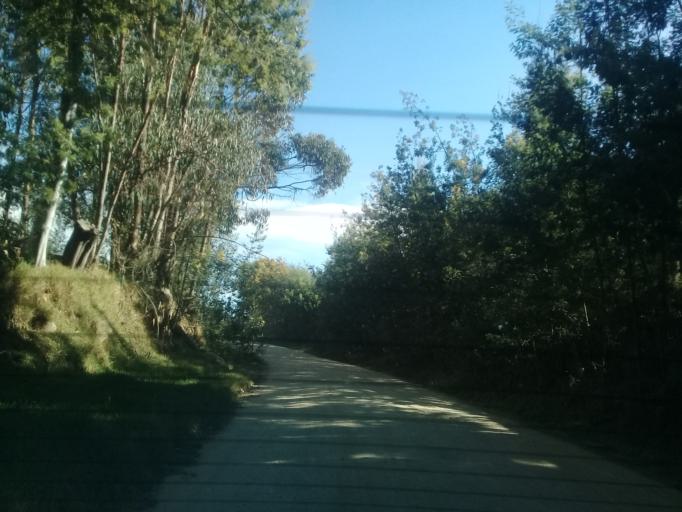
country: CO
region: Cundinamarca
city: Tocancipa
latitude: 4.9276
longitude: -73.8818
